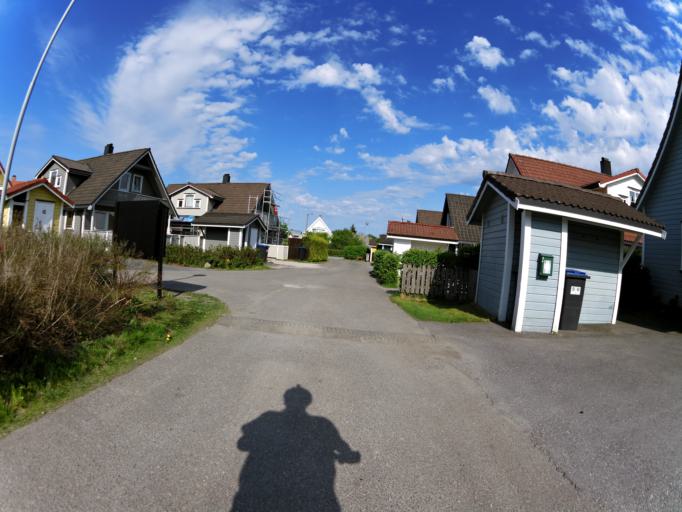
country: NO
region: Ostfold
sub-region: Fredrikstad
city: Fredrikstad
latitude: 59.2327
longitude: 10.9698
